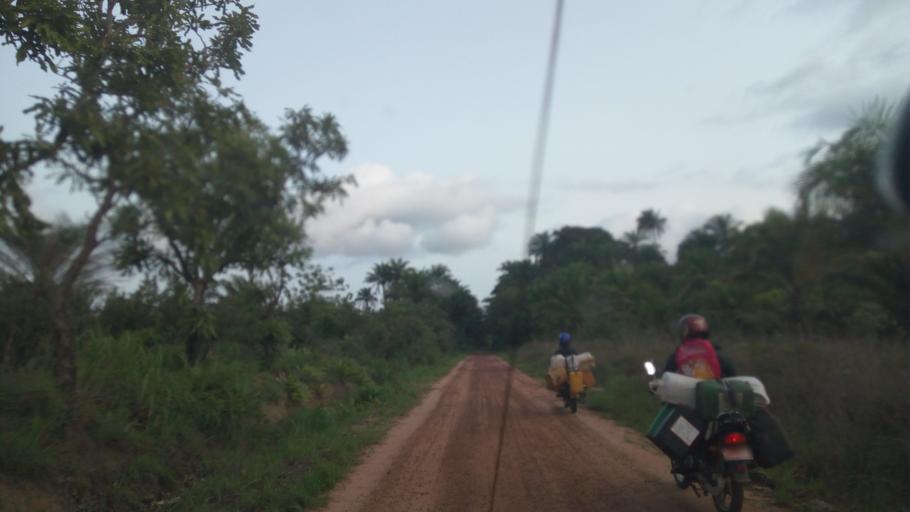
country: SL
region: Northern Province
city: Mambolo
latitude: 9.0027
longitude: -13.0128
